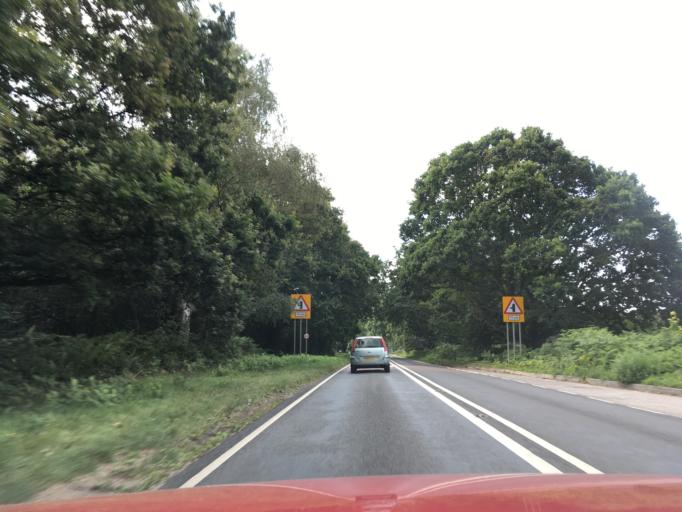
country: GB
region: England
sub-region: Hampshire
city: Wickham
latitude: 50.9142
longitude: -1.2003
